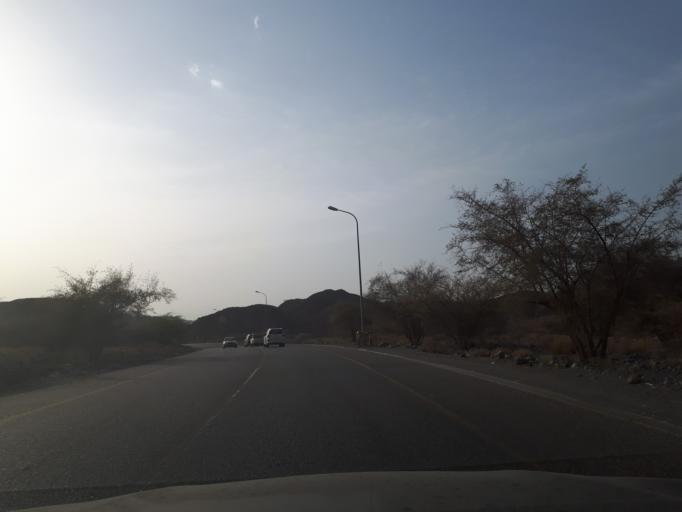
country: OM
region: Muhafazat ad Dakhiliyah
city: Sufalat Sama'il
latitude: 23.1691
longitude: 58.1017
